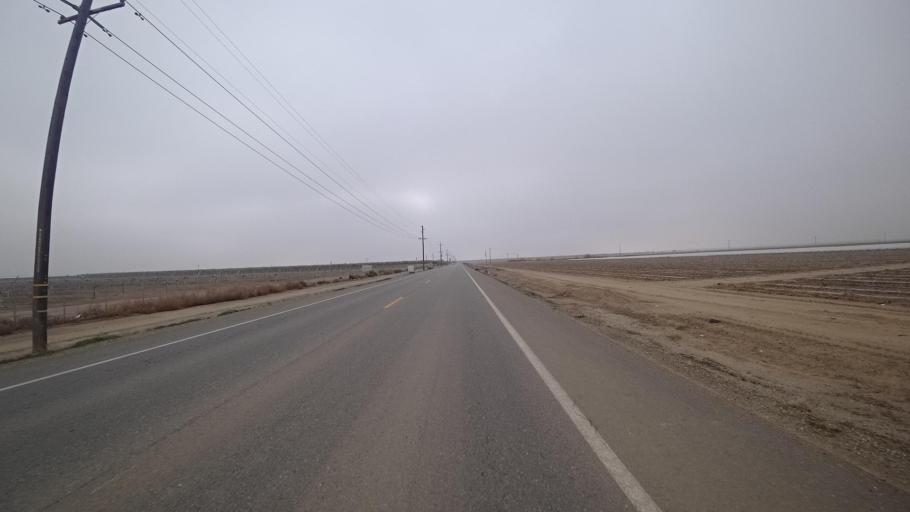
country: US
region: California
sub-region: Kern County
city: Greenfield
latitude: 35.1047
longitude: -119.1097
